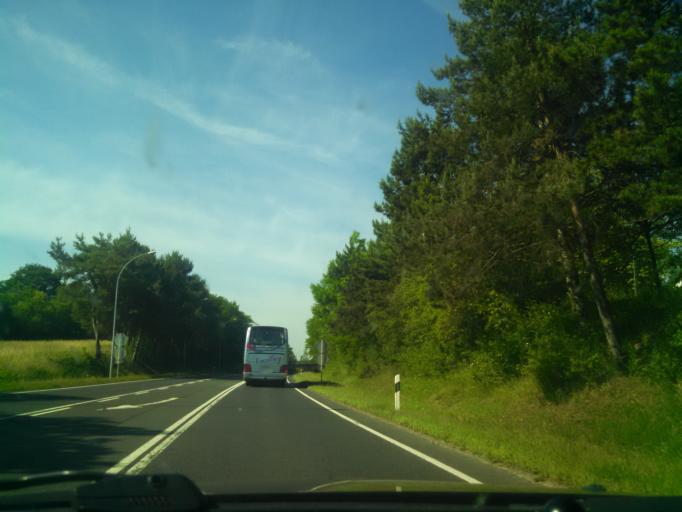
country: LU
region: Grevenmacher
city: Gonderange
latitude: 49.6956
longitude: 6.2452
